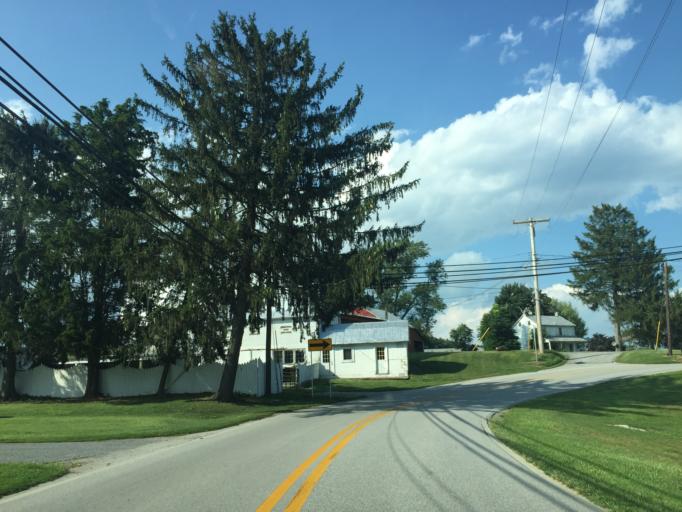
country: US
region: Maryland
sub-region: Carroll County
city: Manchester
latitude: 39.6507
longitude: -76.8639
